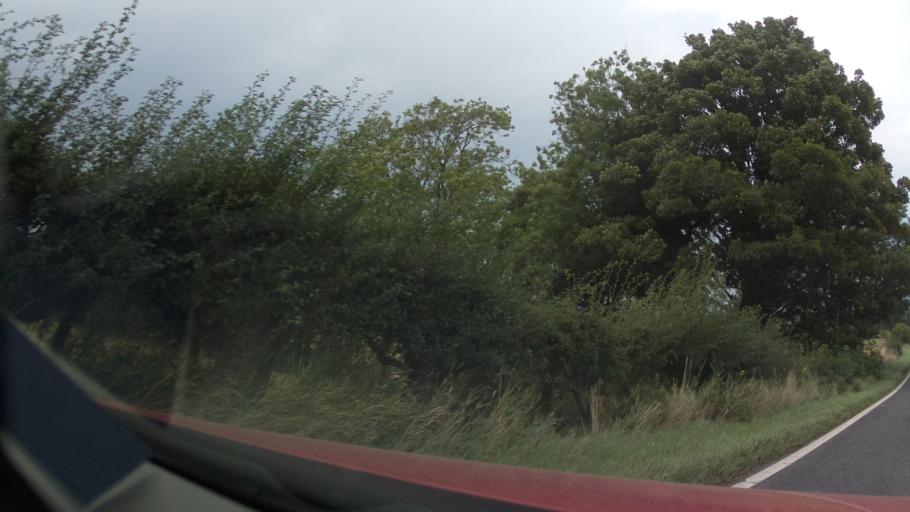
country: GB
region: Scotland
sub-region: Dumfries and Galloway
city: Locharbriggs
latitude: 55.0647
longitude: -3.5042
